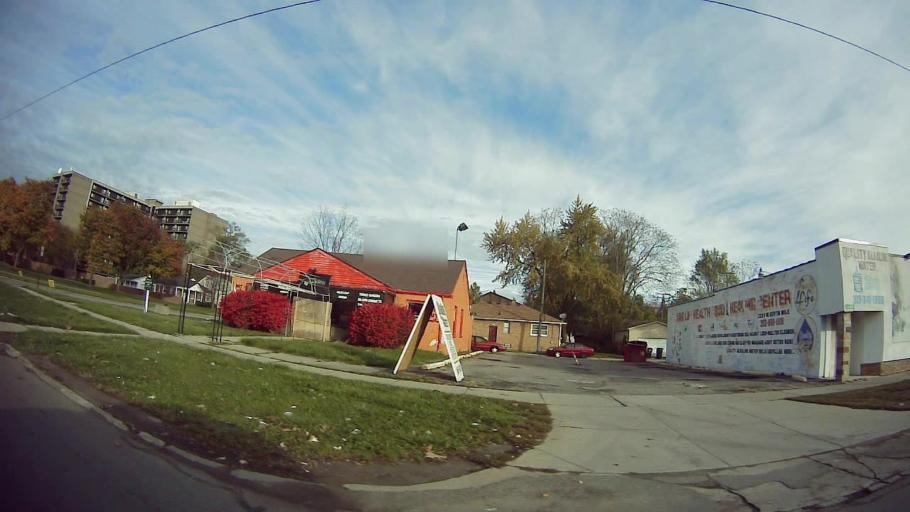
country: US
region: Michigan
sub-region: Oakland County
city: Oak Park
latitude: 42.4305
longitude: -83.1972
